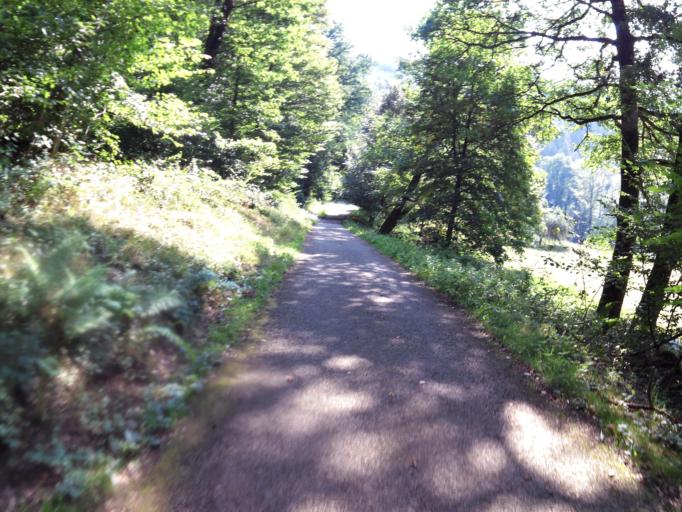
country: DE
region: Rheinland-Pfalz
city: Dahlem
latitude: 49.9179
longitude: 6.6112
